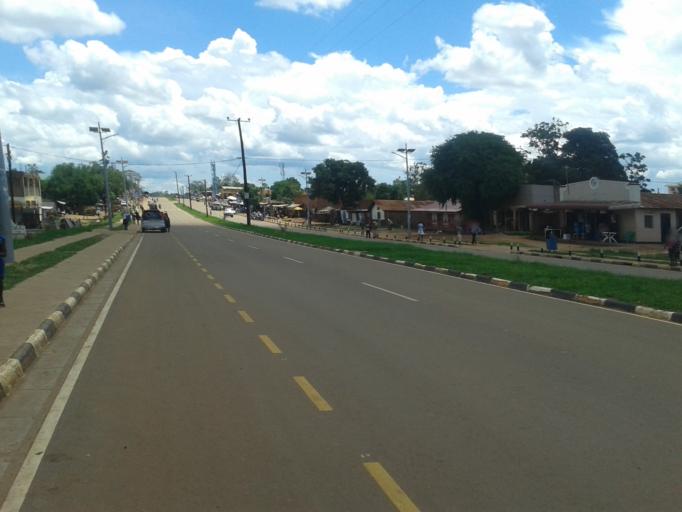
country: UG
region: Northern Region
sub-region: Gulu District
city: Gulu
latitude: 2.7645
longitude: 32.3018
